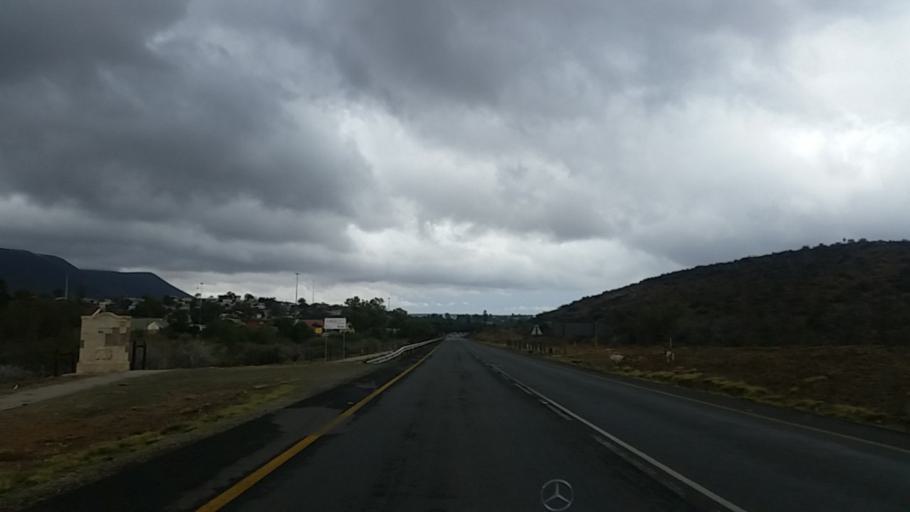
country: ZA
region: Eastern Cape
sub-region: Cacadu District Municipality
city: Graaff-Reinet
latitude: -32.2399
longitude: 24.5365
